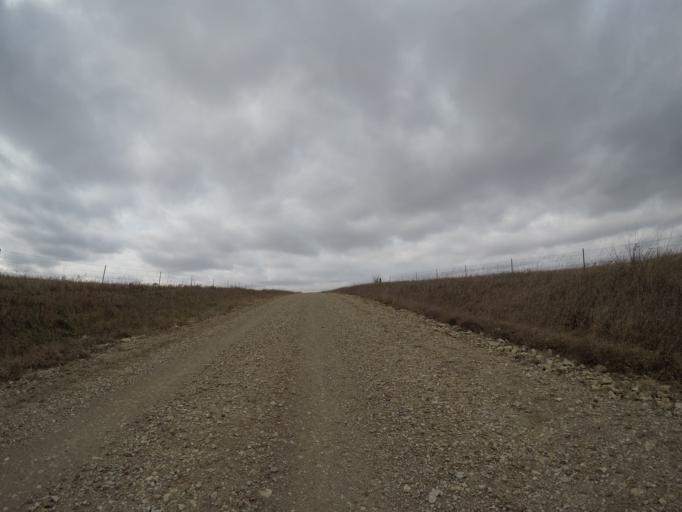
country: US
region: Kansas
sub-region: Morris County
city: Council Grove
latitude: 38.7244
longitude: -96.2057
